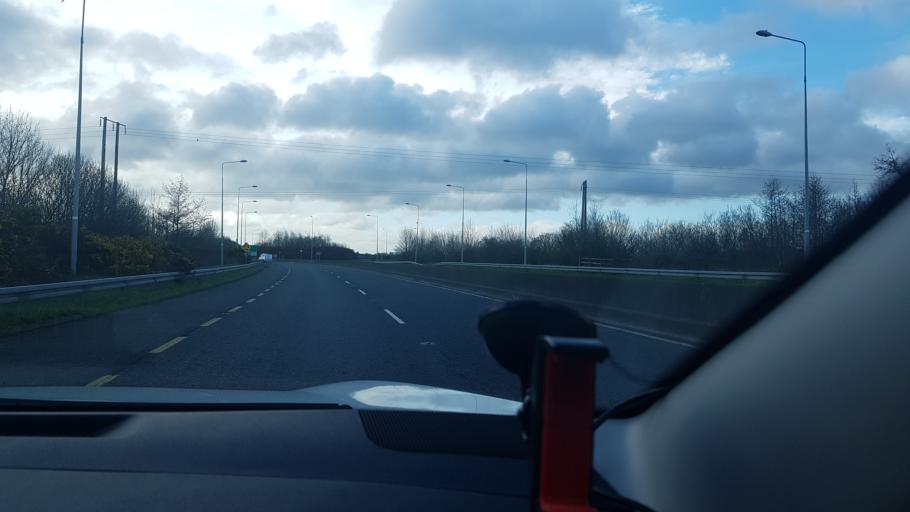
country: IE
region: Leinster
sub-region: Lu
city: Dundalk
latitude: 54.0318
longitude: -6.3856
